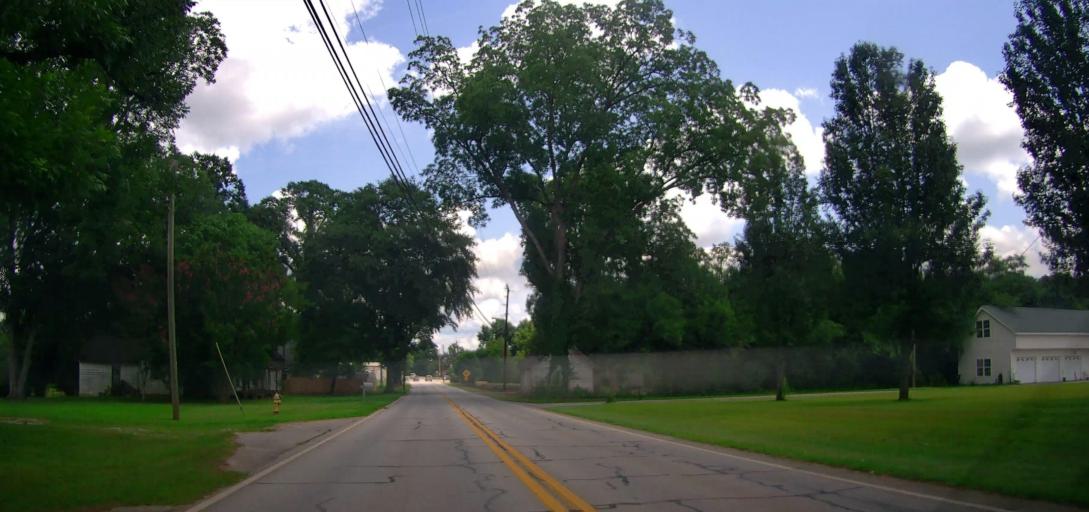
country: US
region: Georgia
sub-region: Troup County
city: Hogansville
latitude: 33.2312
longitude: -84.9473
